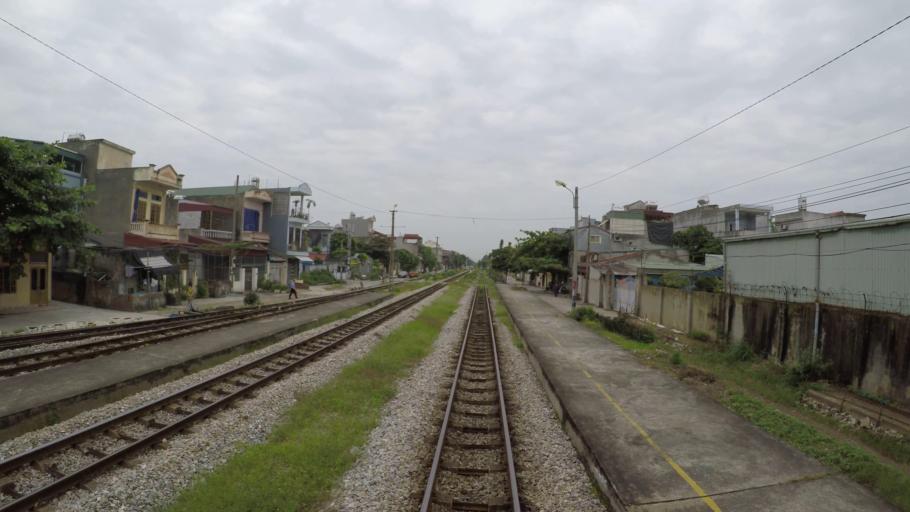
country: VN
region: Hai Duong
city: Thanh Pho Hai Duong
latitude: 20.9484
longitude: 106.3224
